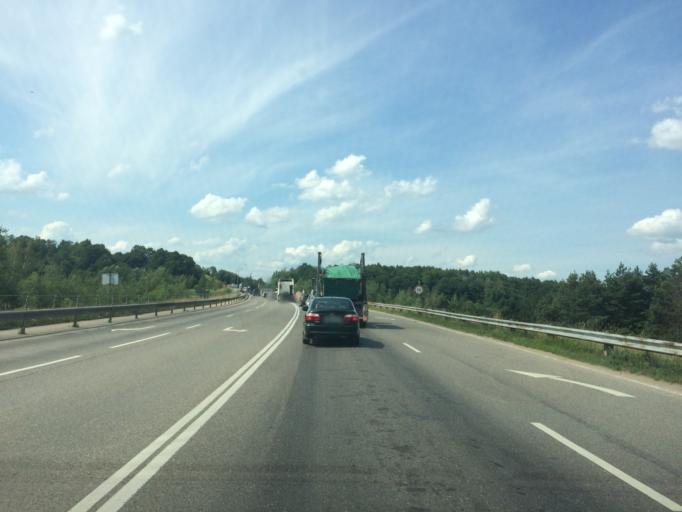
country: LT
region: Kauno apskritis
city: Jonava
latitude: 55.0853
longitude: 24.3171
